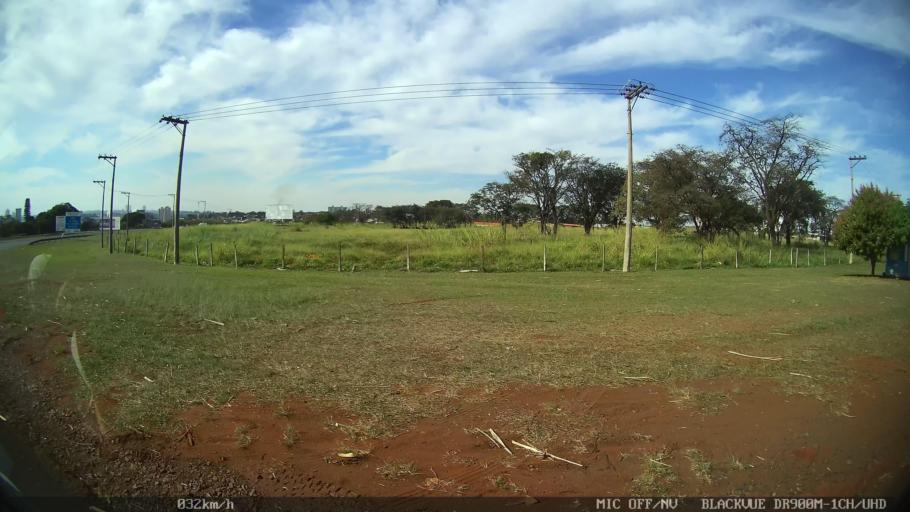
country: BR
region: Sao Paulo
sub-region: Araraquara
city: Araraquara
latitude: -21.8179
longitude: -48.1773
